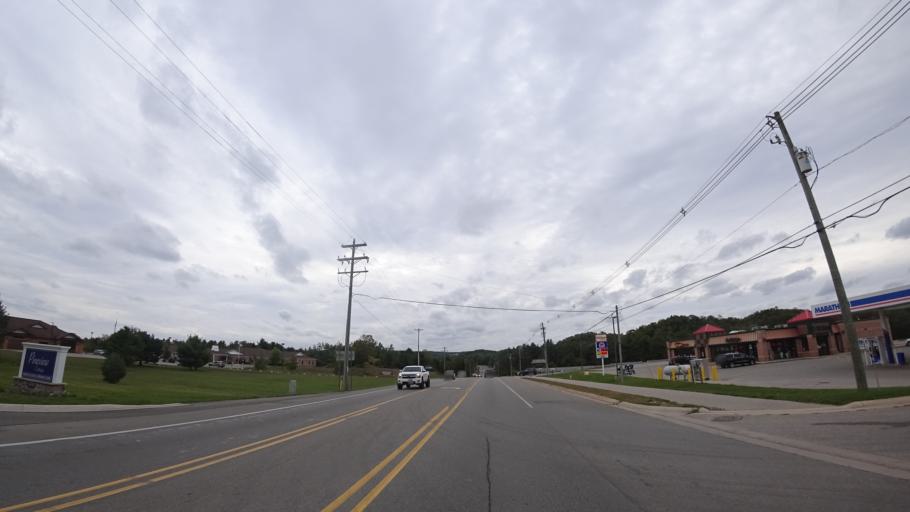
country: US
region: Michigan
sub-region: Emmet County
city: Petoskey
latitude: 45.4206
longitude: -84.9045
